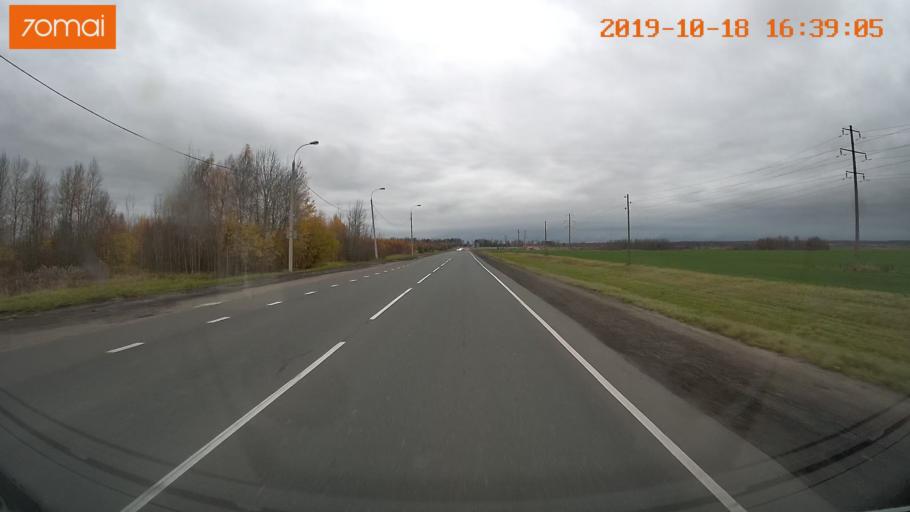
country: RU
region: Vladimir
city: Suzdal'
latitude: 56.4453
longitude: 40.4639
